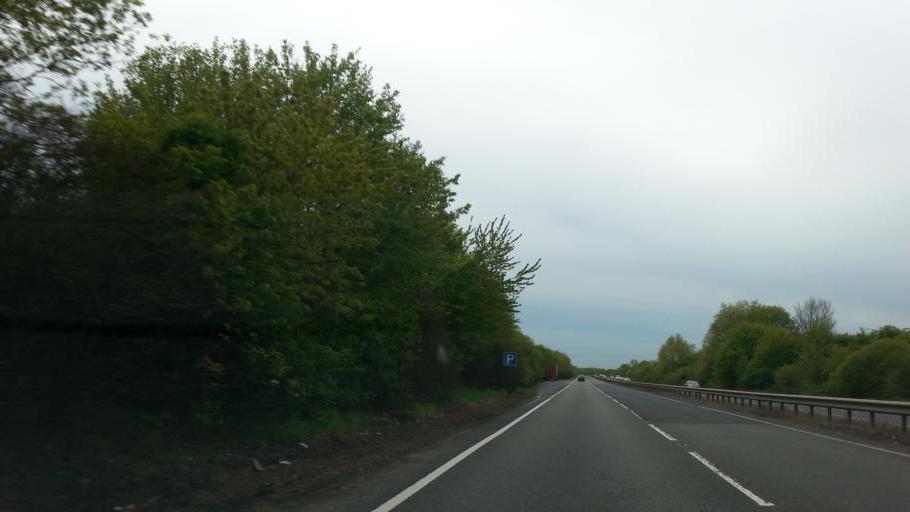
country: GB
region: England
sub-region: Peterborough
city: Castor
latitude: 52.5744
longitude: -0.3331
